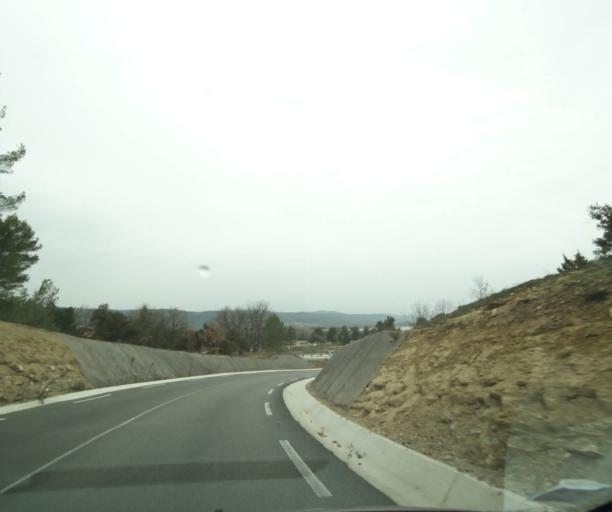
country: FR
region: Provence-Alpes-Cote d'Azur
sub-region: Departement du Vaucluse
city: Beaumont-de-Pertuis
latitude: 43.6954
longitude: 5.7335
